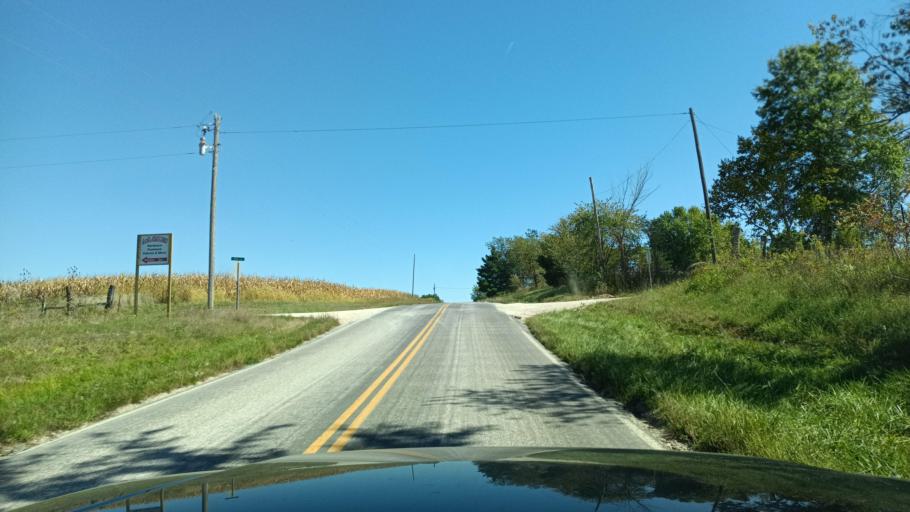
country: US
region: Missouri
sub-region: Macon County
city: La Plata
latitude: 40.0225
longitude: -92.5671
